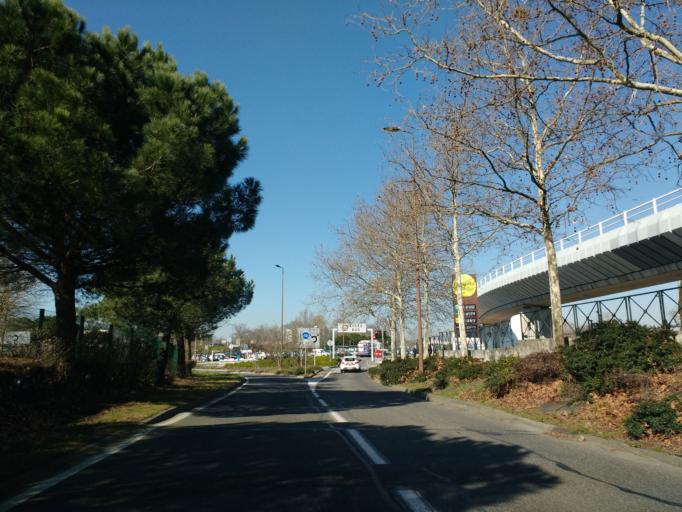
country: FR
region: Midi-Pyrenees
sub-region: Departement de la Haute-Garonne
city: Portet-sur-Garonne
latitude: 43.5686
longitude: 1.3924
